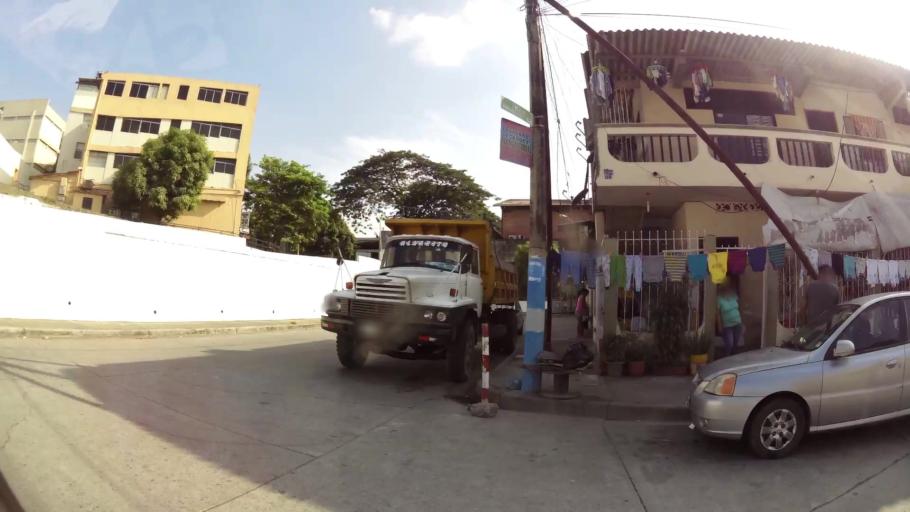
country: EC
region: Guayas
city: Guayaquil
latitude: -2.1838
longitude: -79.9045
